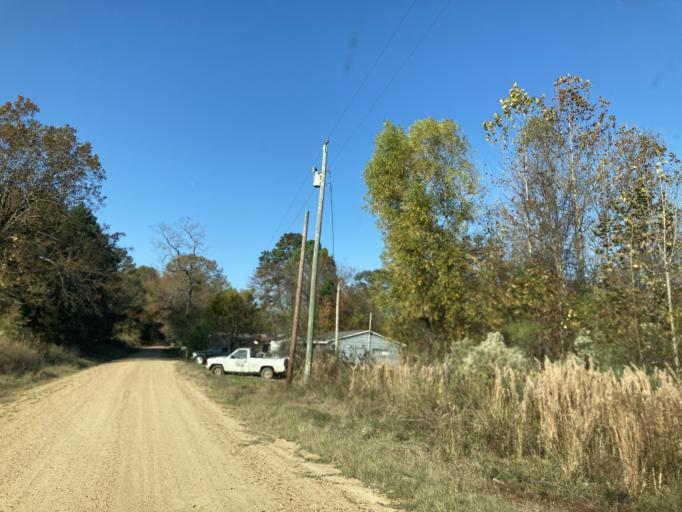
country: US
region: Mississippi
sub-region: Madison County
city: Kearney Park
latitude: 32.7348
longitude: -90.3068
